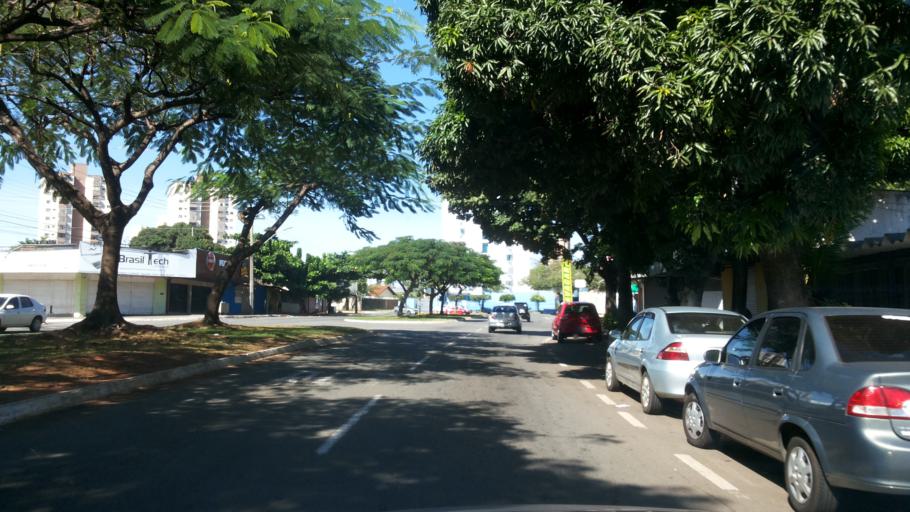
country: BR
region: Goias
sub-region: Goiania
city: Goiania
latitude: -16.7110
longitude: -49.2513
